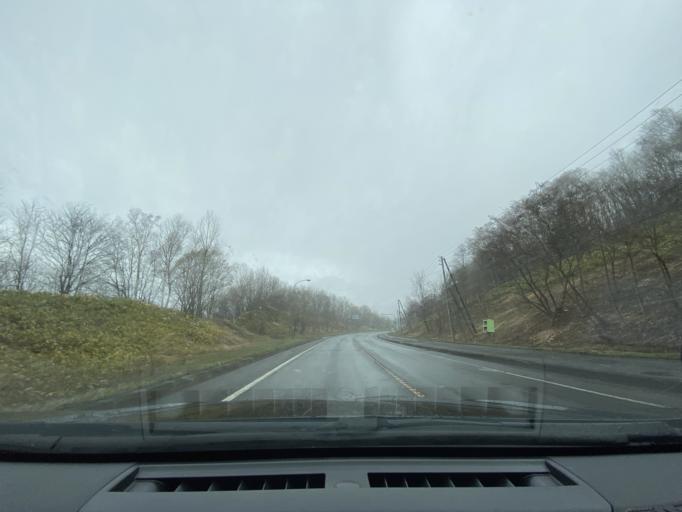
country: JP
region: Hokkaido
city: Fukagawa
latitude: 43.7151
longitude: 142.1745
